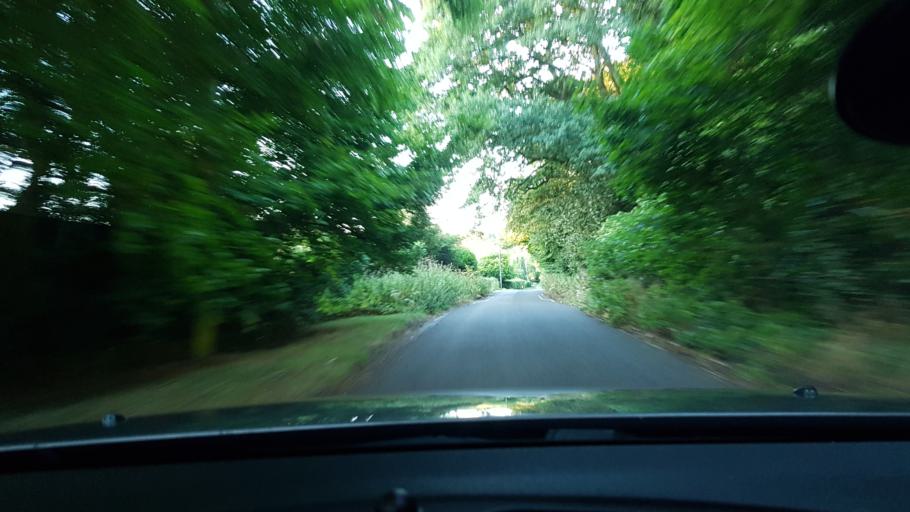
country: GB
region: England
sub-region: West Berkshire
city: Hungerford
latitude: 51.3978
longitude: -1.5182
